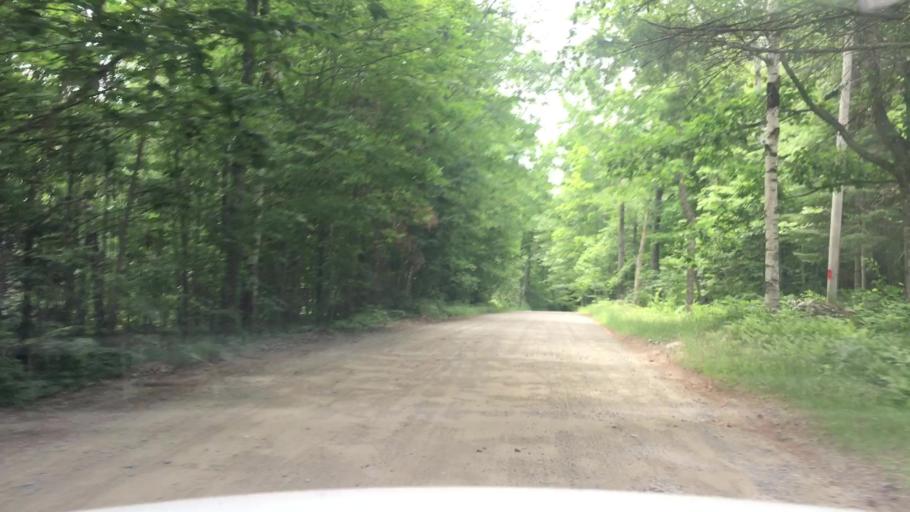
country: US
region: Maine
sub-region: Waldo County
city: Searsmont
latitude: 44.4220
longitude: -69.2583
